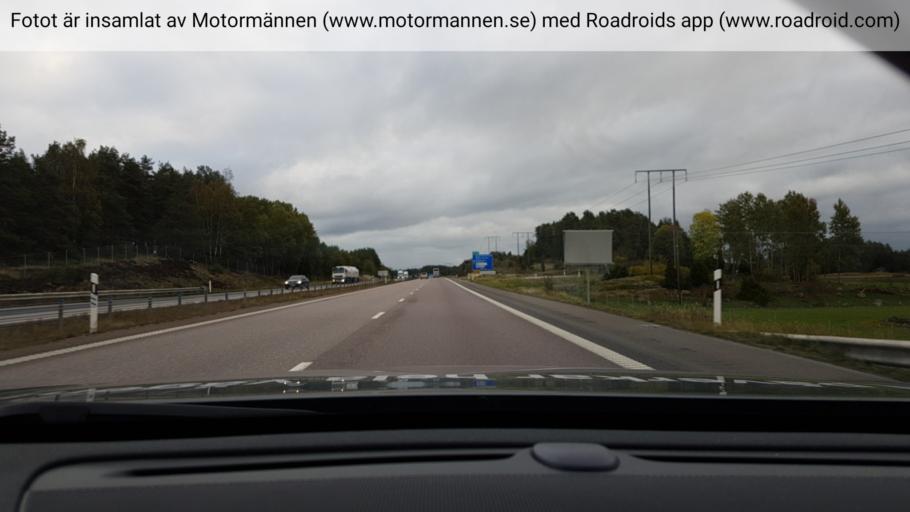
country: SE
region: OEstergoetland
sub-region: Norrkopings Kommun
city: Kimstad
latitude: 58.4874
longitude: 15.9270
